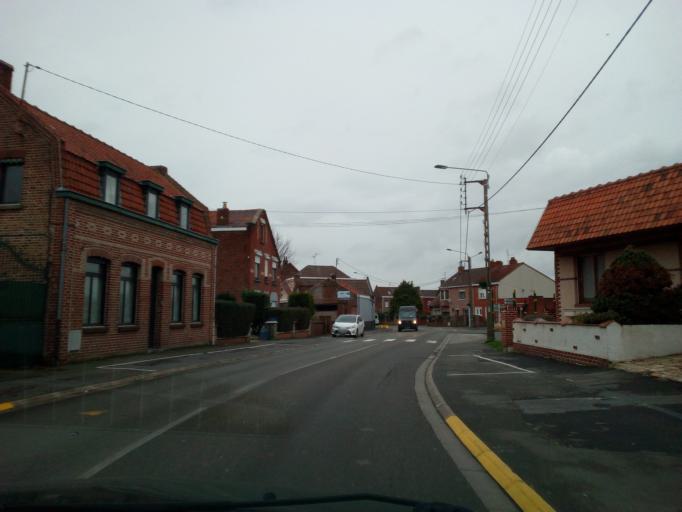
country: FR
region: Nord-Pas-de-Calais
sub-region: Departement du Nord
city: Bauvin
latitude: 50.5181
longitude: 2.8916
